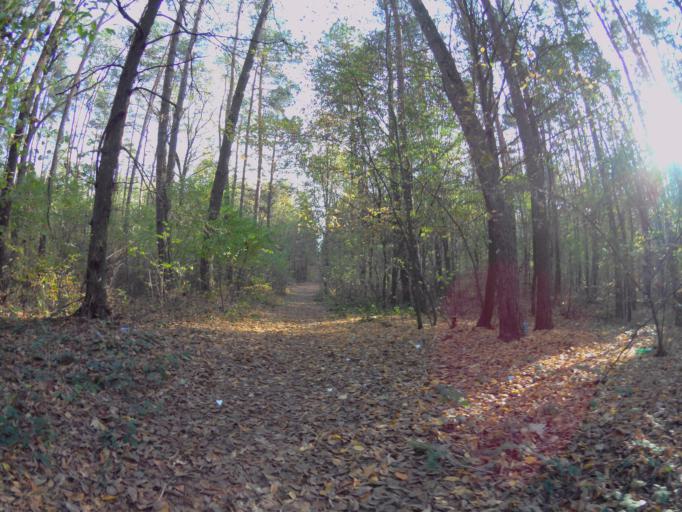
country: PL
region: Subcarpathian Voivodeship
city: Nowa Sarzyna
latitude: 50.3136
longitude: 22.3440
